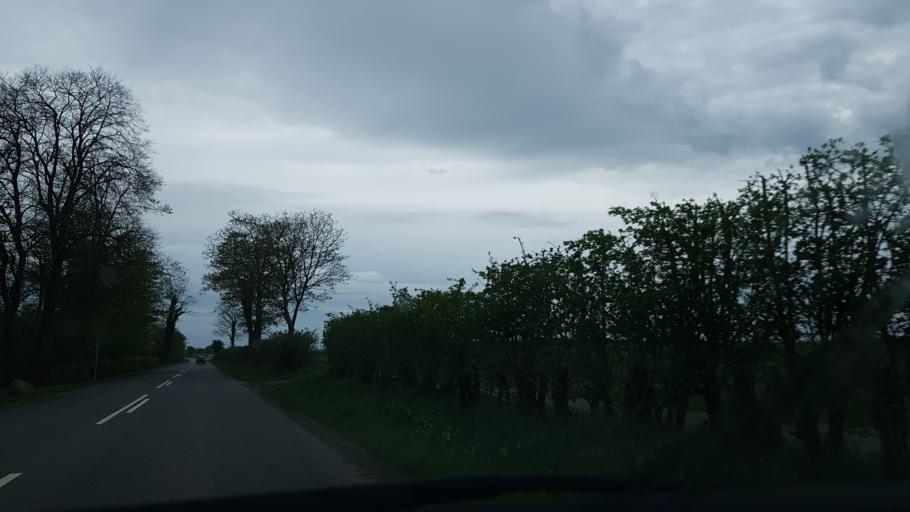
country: DK
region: South Denmark
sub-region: Kolding Kommune
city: Lunderskov
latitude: 55.4640
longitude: 9.3328
